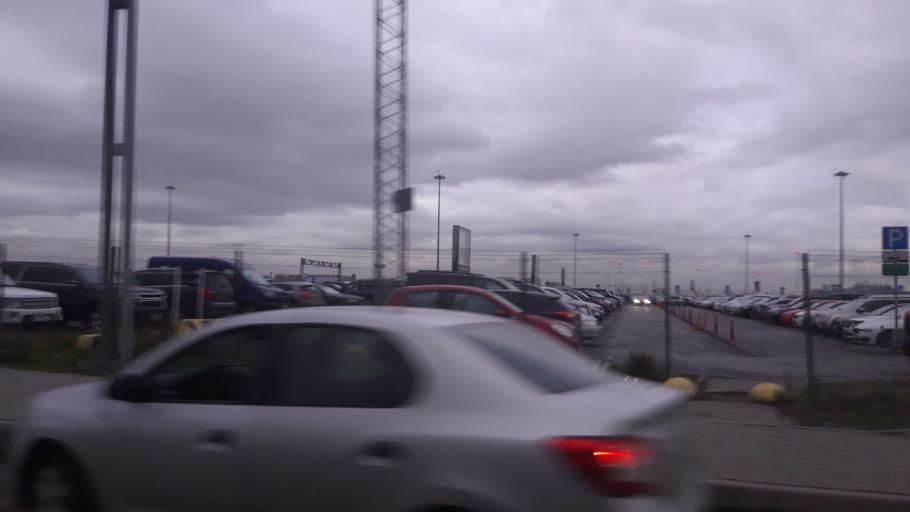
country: RU
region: St.-Petersburg
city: Dachnoye
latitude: 59.7975
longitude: 30.2800
